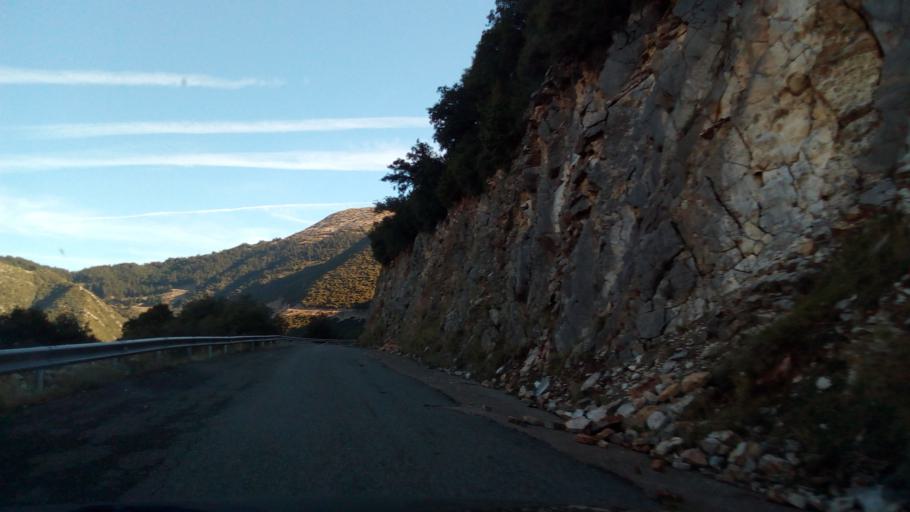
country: GR
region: West Greece
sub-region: Nomos Aitolias kai Akarnanias
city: Nafpaktos
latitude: 38.5098
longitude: 21.8424
